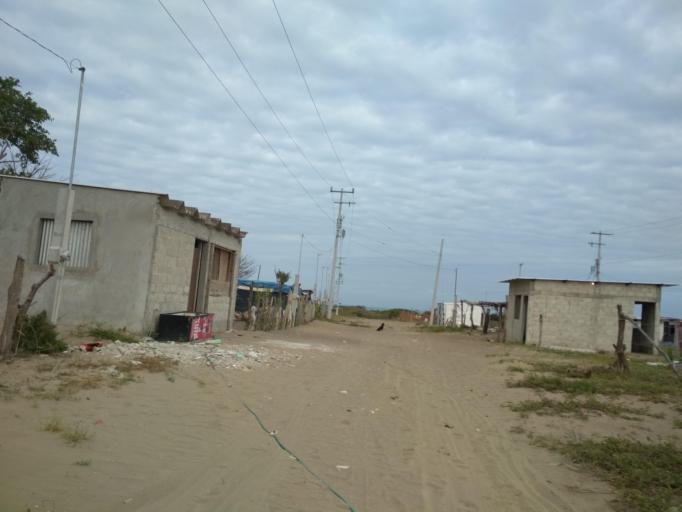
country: MX
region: Veracruz
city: Anton Lizardo
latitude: 19.0451
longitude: -95.9916
